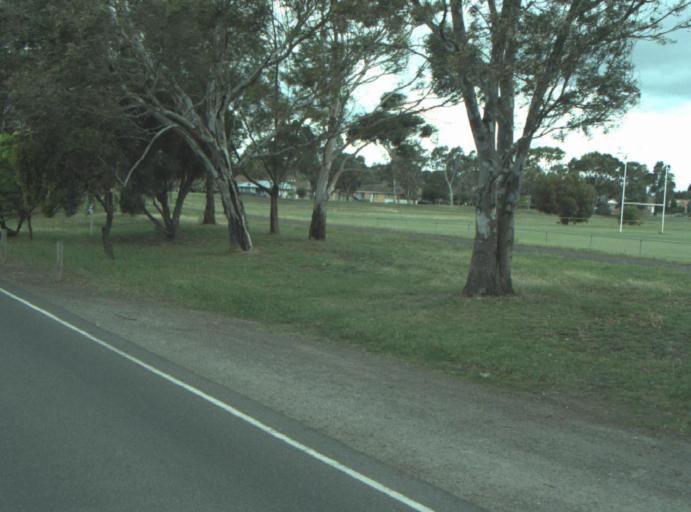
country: AU
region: Victoria
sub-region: Greater Geelong
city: Bell Park
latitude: -38.0661
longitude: 144.3677
